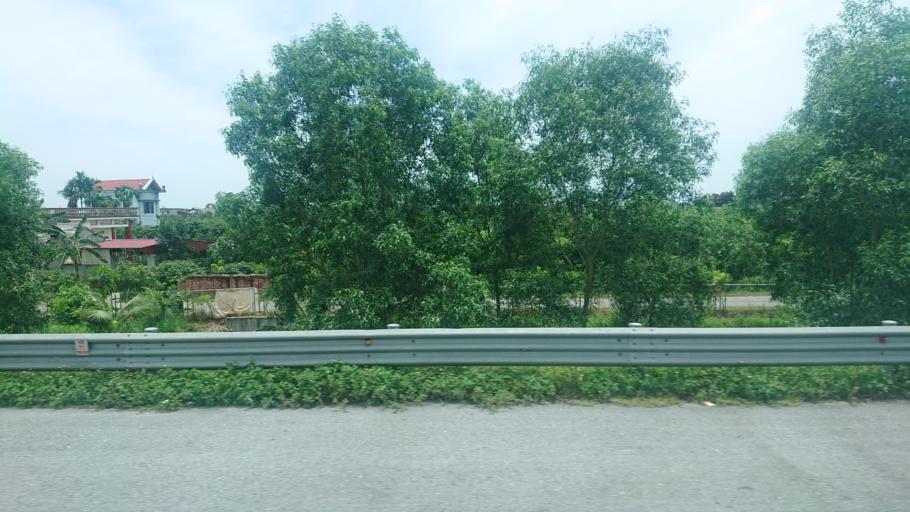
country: VN
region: Hai Phong
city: An Lao
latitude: 20.8112
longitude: 106.5042
